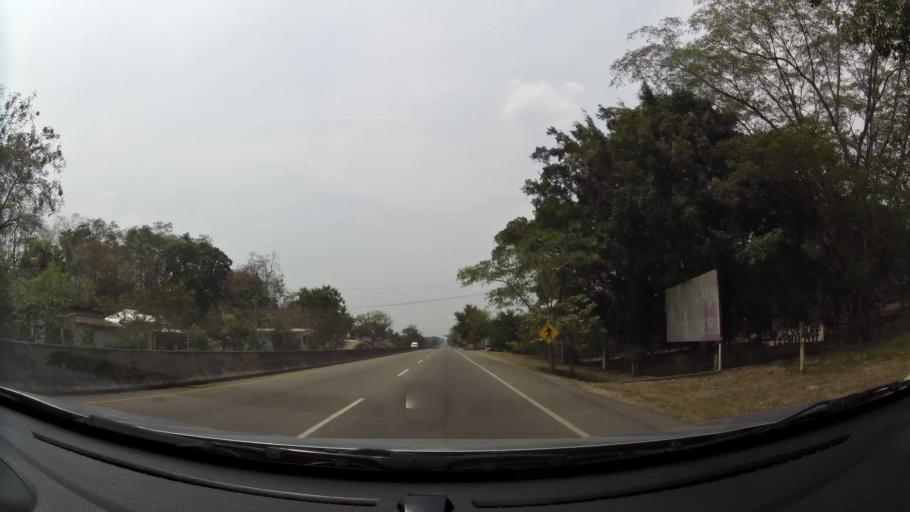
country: HN
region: Cortes
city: Oropendolas
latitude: 15.0575
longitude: -87.9288
